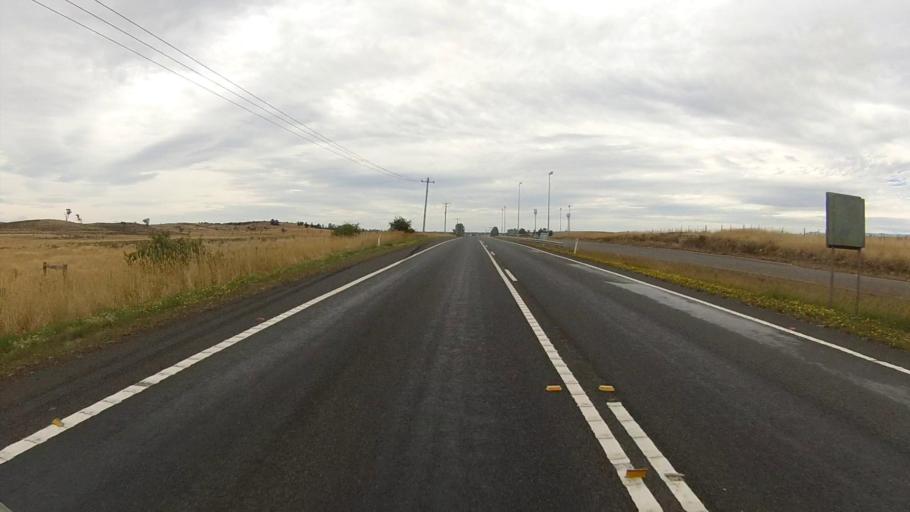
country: AU
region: Tasmania
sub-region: Northern Midlands
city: Evandale
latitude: -41.8858
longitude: 147.4677
